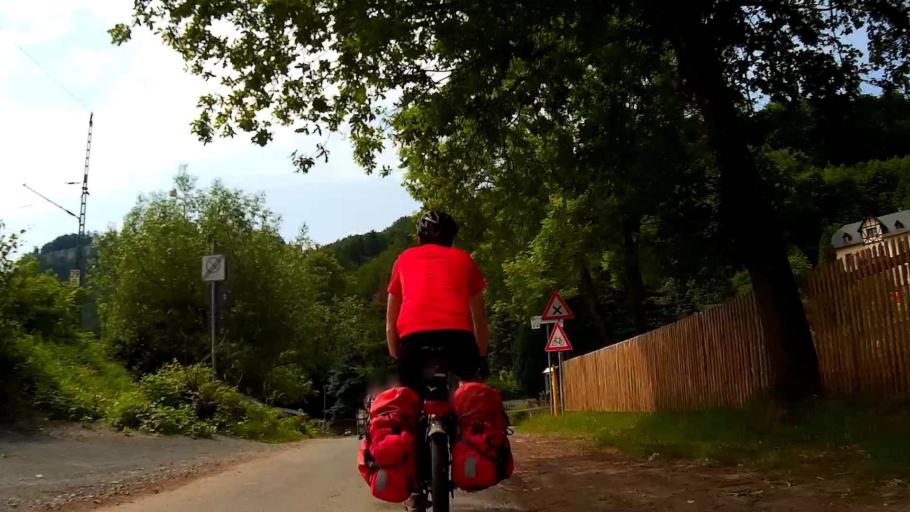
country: DE
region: Saxony
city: Konigstein
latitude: 50.9292
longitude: 14.0554
